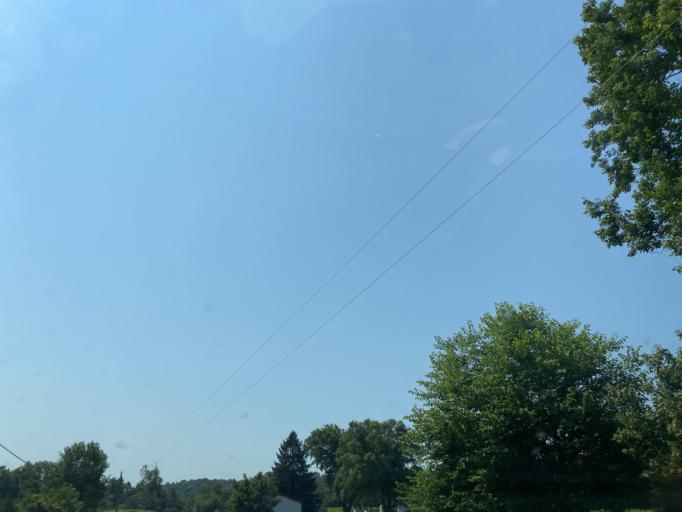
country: US
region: Kentucky
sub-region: Campbell County
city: Claryville
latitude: 38.8281
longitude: -84.4568
